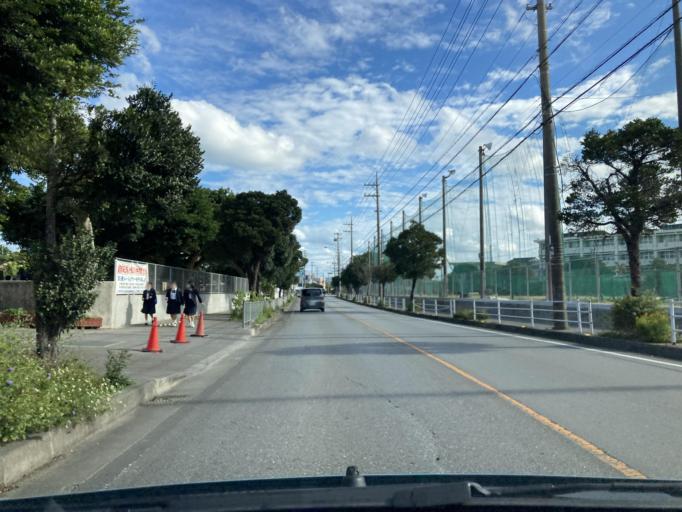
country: JP
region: Okinawa
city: Ishikawa
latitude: 26.4167
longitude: 127.8201
